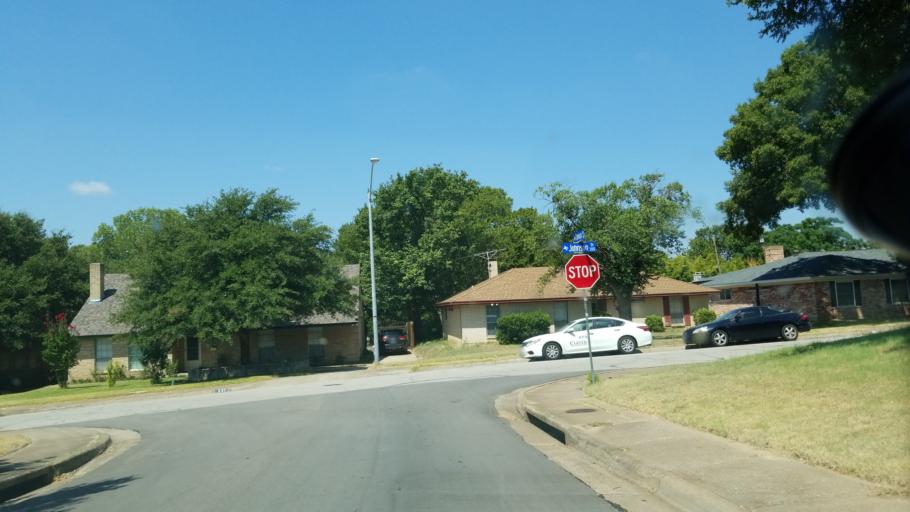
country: US
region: Texas
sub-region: Dallas County
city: Duncanville
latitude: 32.6542
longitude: -96.8991
